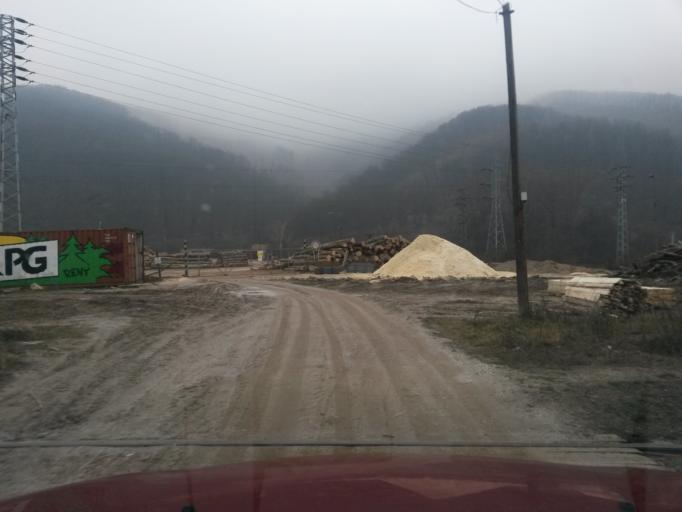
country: SK
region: Kosicky
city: Roznava
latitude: 48.6990
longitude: 20.5010
